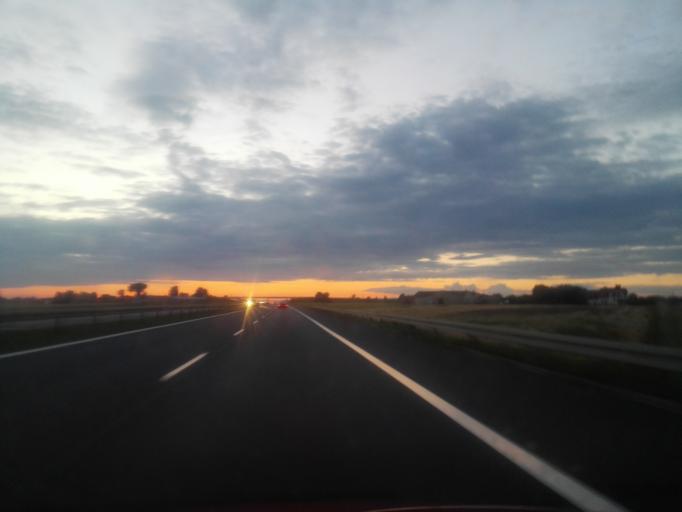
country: PL
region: Lodz Voivodeship
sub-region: Powiat piotrkowski
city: Moszczenica
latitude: 51.4723
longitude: 19.6304
